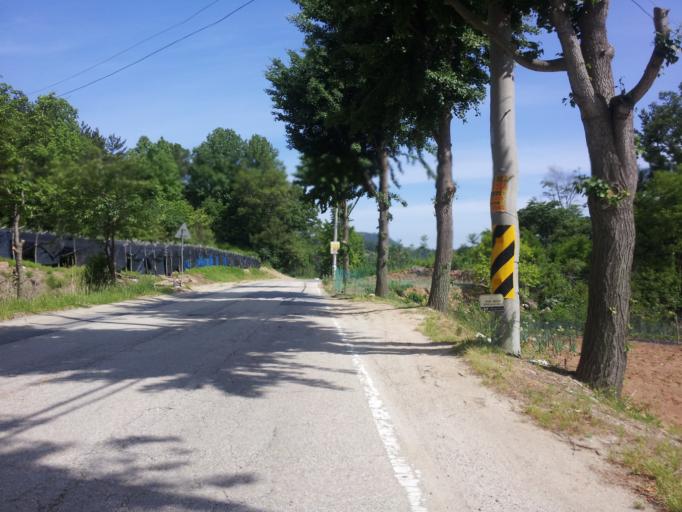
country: KR
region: Daejeon
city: Daejeon
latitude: 36.3407
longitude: 127.4788
